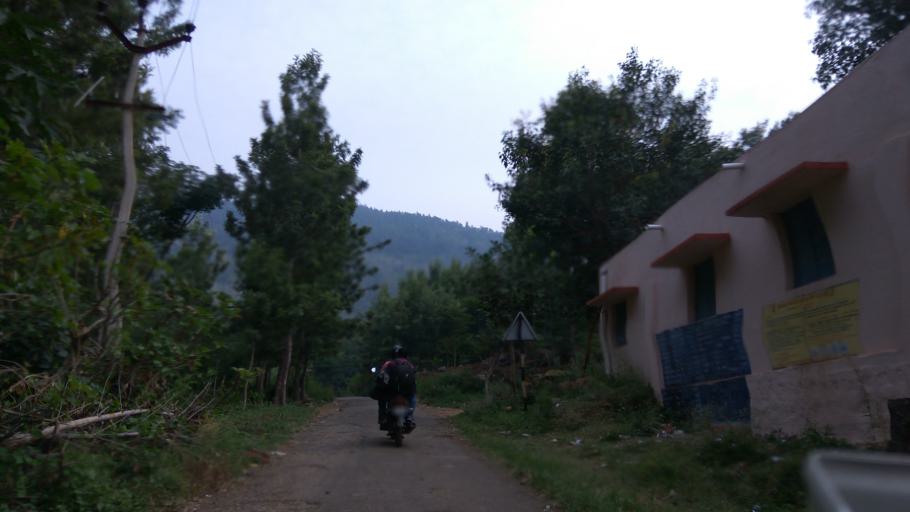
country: IN
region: Tamil Nadu
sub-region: Dharmapuri
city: Mallapuram
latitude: 11.8637
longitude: 78.1908
